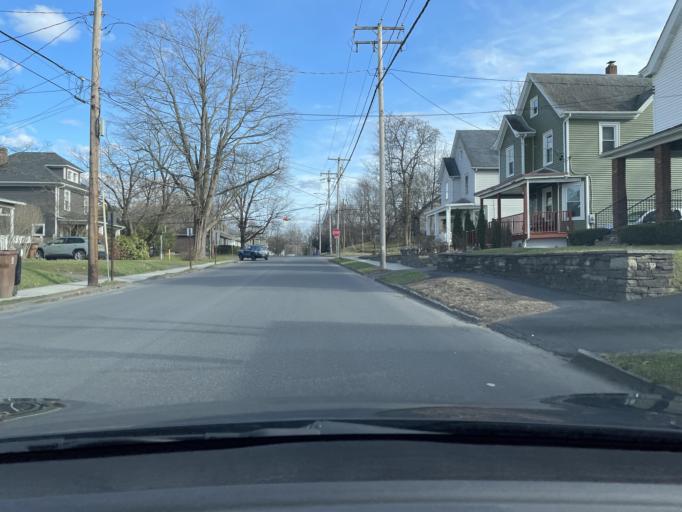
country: US
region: New York
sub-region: Ulster County
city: Kingston
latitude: 41.9243
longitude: -74.0149
